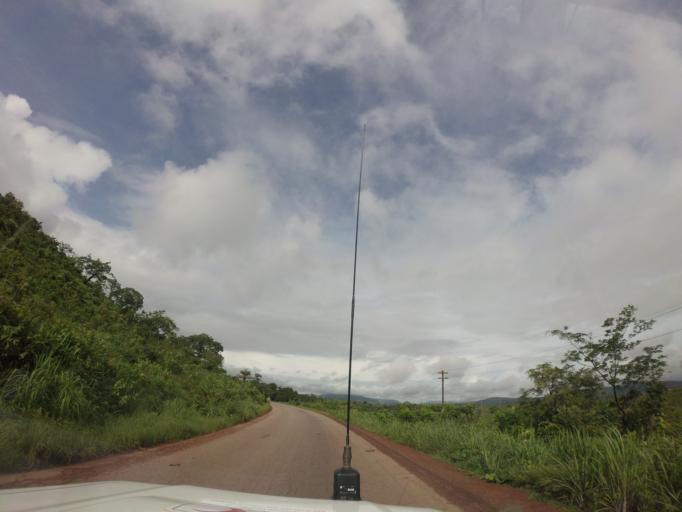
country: GN
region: Kindia
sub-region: Coyah
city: Coyah
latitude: 9.8254
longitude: -13.2588
